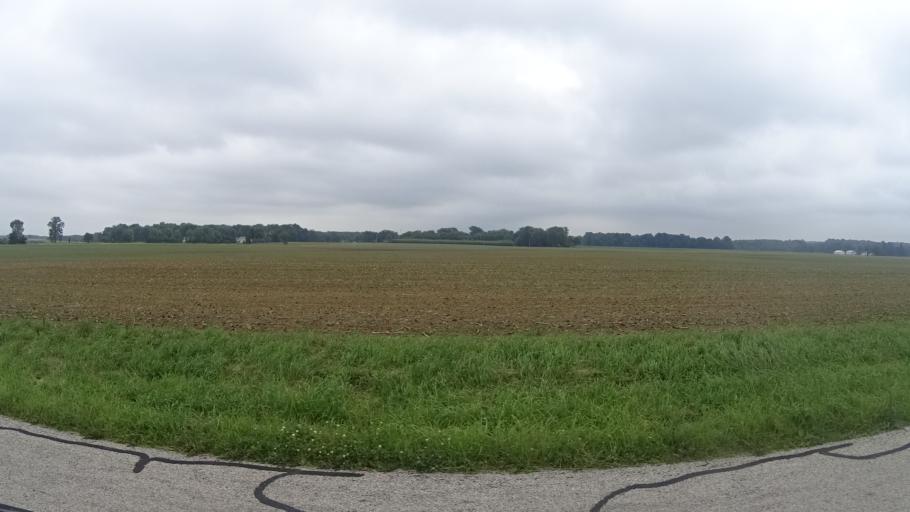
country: US
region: Ohio
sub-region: Erie County
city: Milan
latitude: 41.3198
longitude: -82.5433
